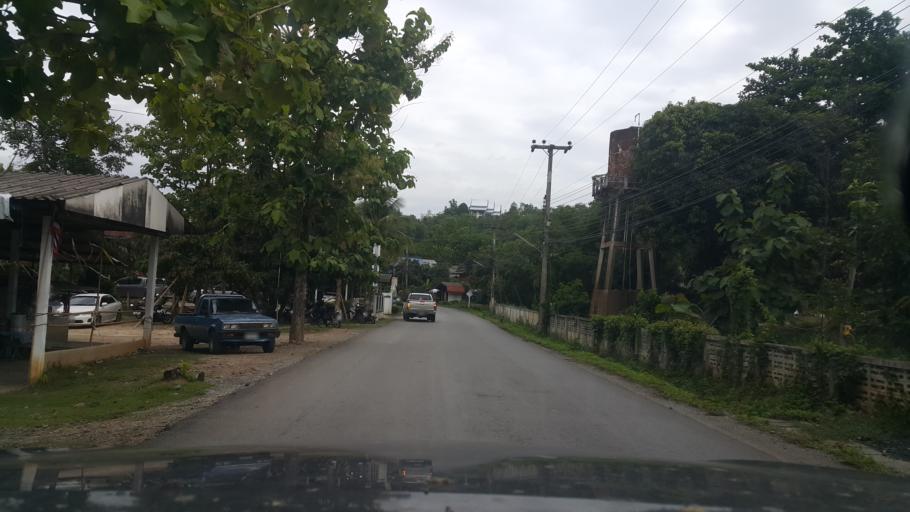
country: TH
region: Chiang Mai
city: San Pa Tong
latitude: 18.6709
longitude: 98.8333
